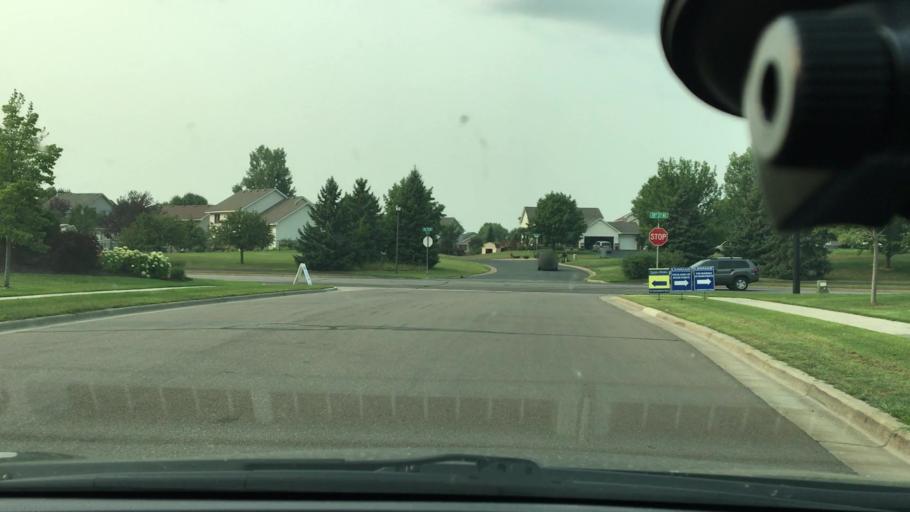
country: US
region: Minnesota
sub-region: Wright County
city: Otsego
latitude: 45.2629
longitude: -93.5720
